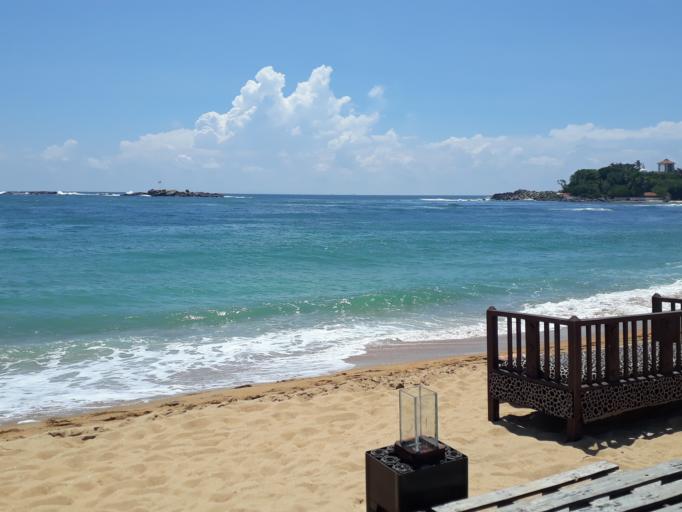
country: LK
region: Southern
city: Unawatuna
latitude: 6.0094
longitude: 80.2470
